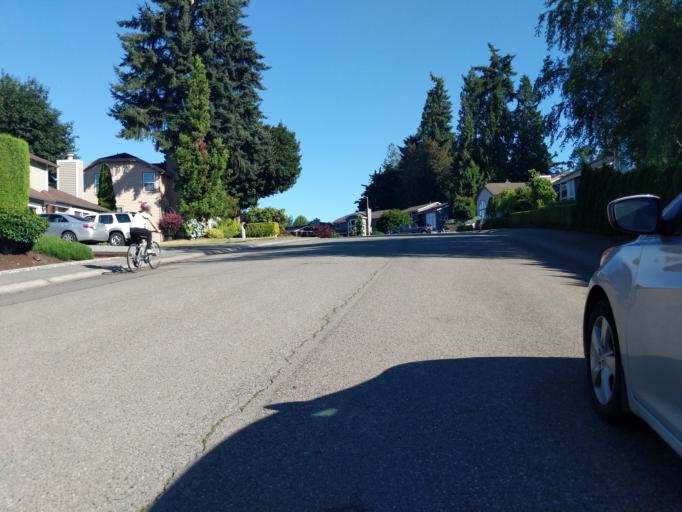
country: US
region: Washington
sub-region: King County
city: Bothell
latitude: 47.7848
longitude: -122.2046
